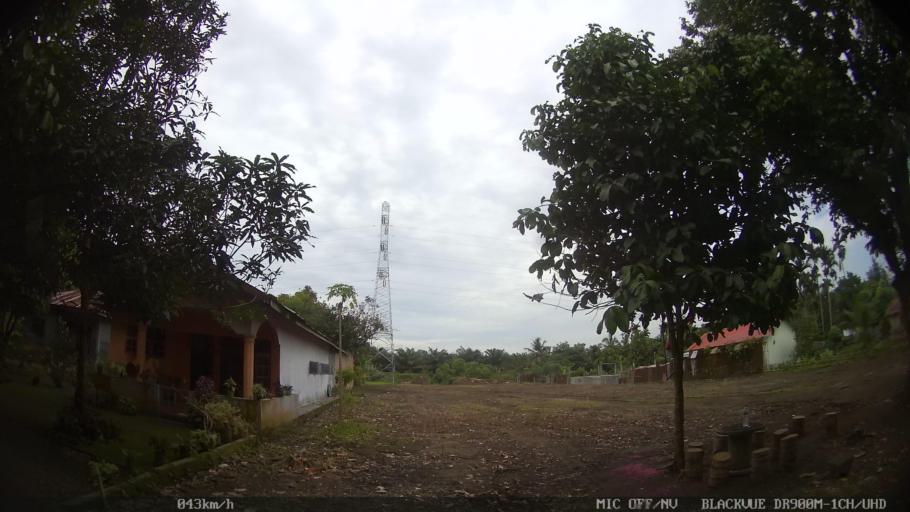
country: ID
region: North Sumatra
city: Sunggal
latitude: 3.6568
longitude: 98.5894
